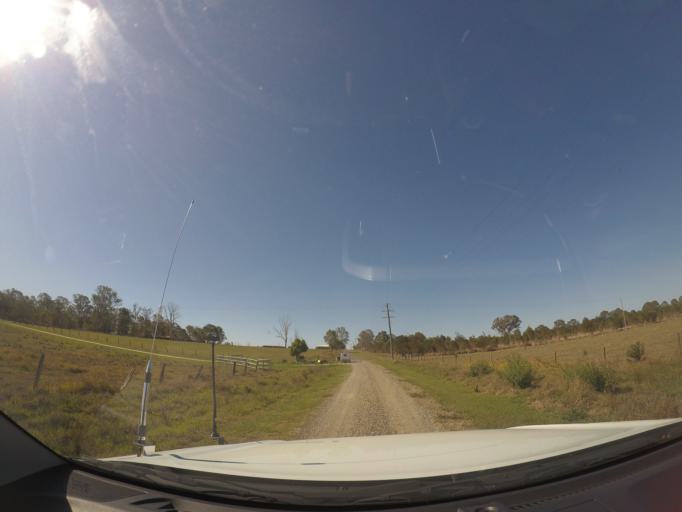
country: AU
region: Queensland
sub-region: Logan
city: North Maclean
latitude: -27.7674
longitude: 153.0470
